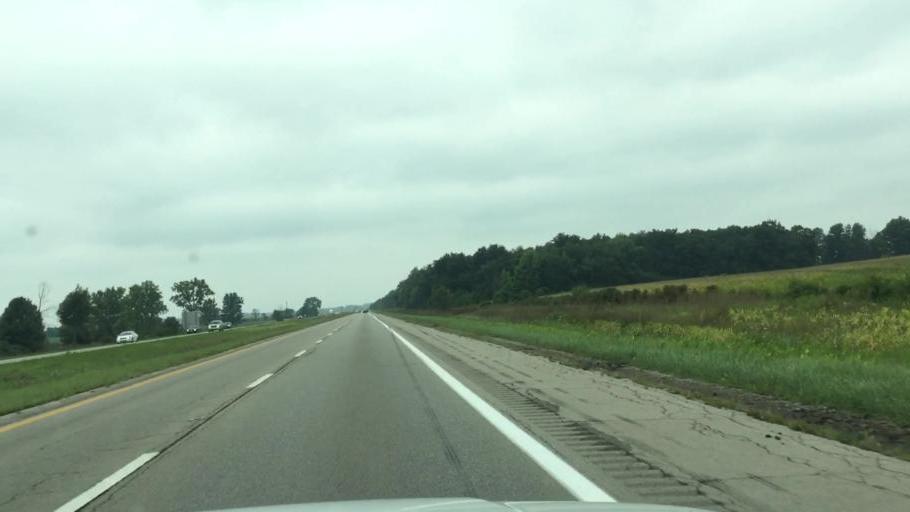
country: US
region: Ohio
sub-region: Union County
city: New California
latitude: 40.1733
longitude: -83.2431
